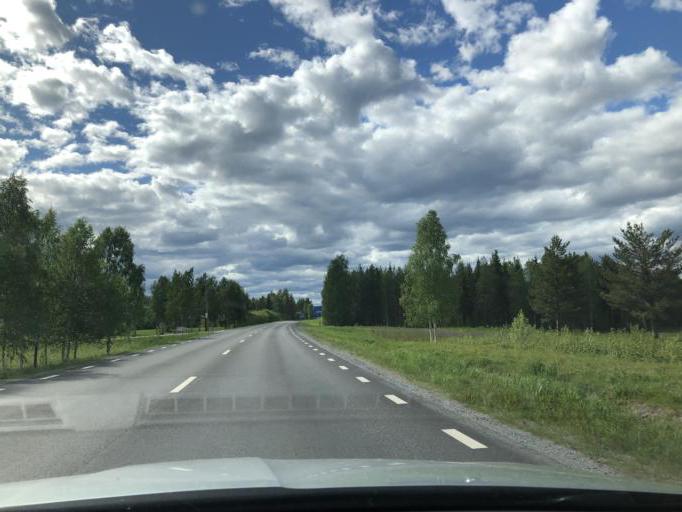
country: SE
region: Norrbotten
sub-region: Alvsbyns Kommun
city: AElvsbyn
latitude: 65.6938
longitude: 20.6593
